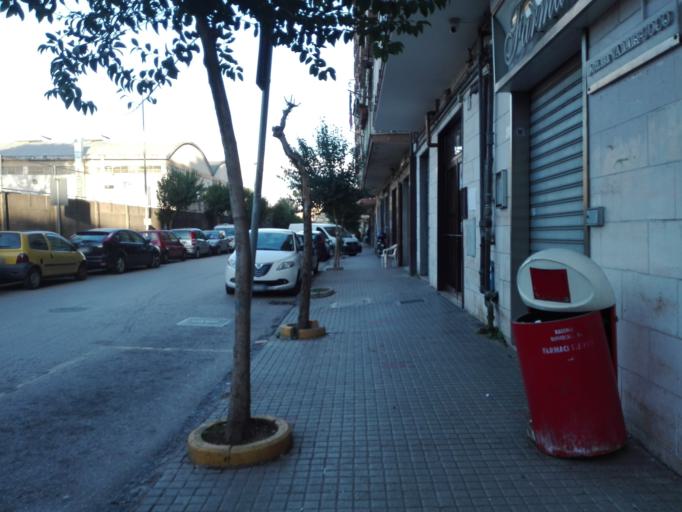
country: IT
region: Campania
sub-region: Provincia di Napoli
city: Casavatore
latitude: 40.8915
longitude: 14.2705
